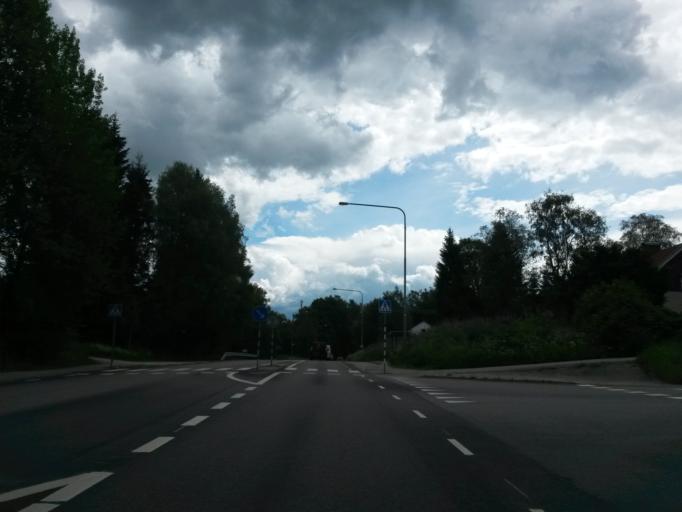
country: SE
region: Vaestra Goetaland
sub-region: Boras Kommun
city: Boras
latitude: 57.7366
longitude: 12.9026
